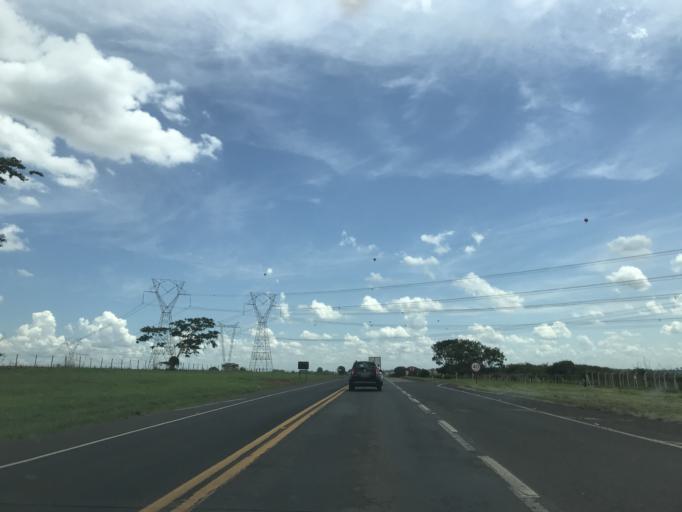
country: BR
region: Sao Paulo
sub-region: Nova Granada
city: Nova Granada
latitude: -20.3335
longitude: -49.2135
